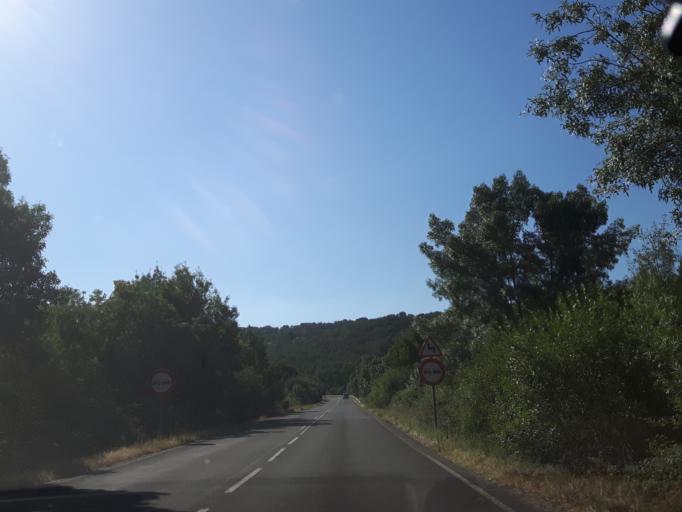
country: ES
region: Castille and Leon
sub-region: Provincia de Salamanca
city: Navalmoral de Bejar
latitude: 40.4169
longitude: -5.8049
